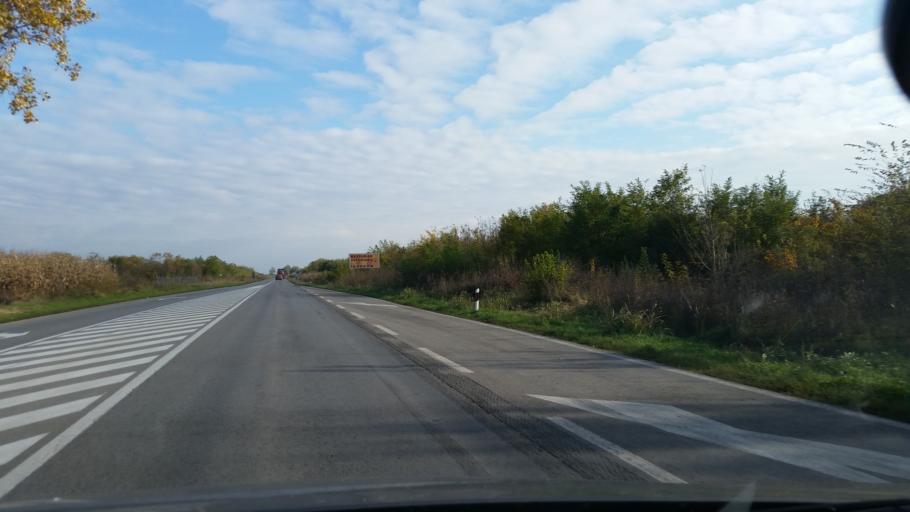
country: RS
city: Ecka
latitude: 45.3307
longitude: 20.4397
